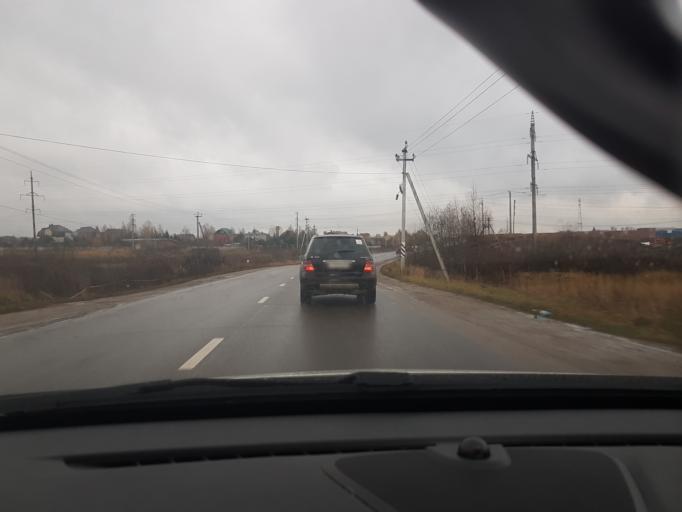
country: RU
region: Moskovskaya
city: Pavlovskaya Sloboda
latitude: 55.8196
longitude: 37.0628
